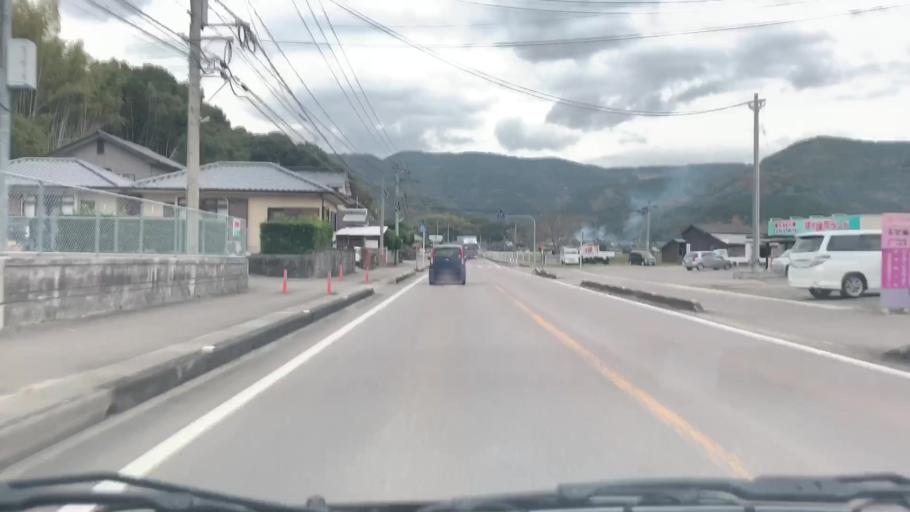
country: JP
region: Saga Prefecture
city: Kashima
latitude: 33.1504
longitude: 130.0640
